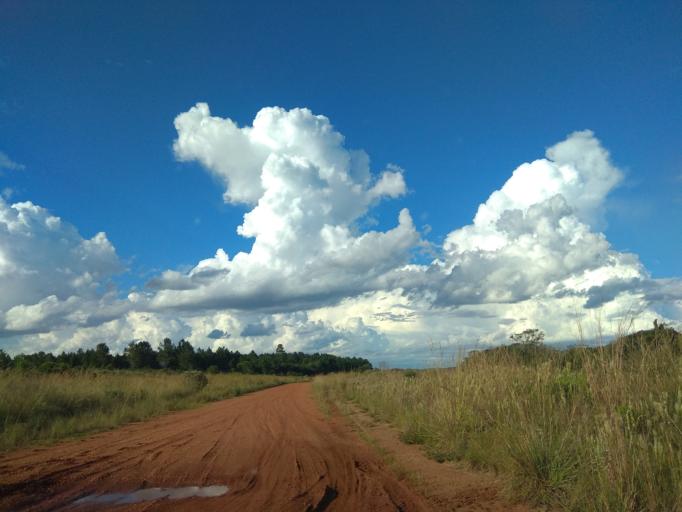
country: AR
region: Misiones
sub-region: Departamento de Candelaria
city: Candelaria
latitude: -27.4953
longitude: -55.7634
